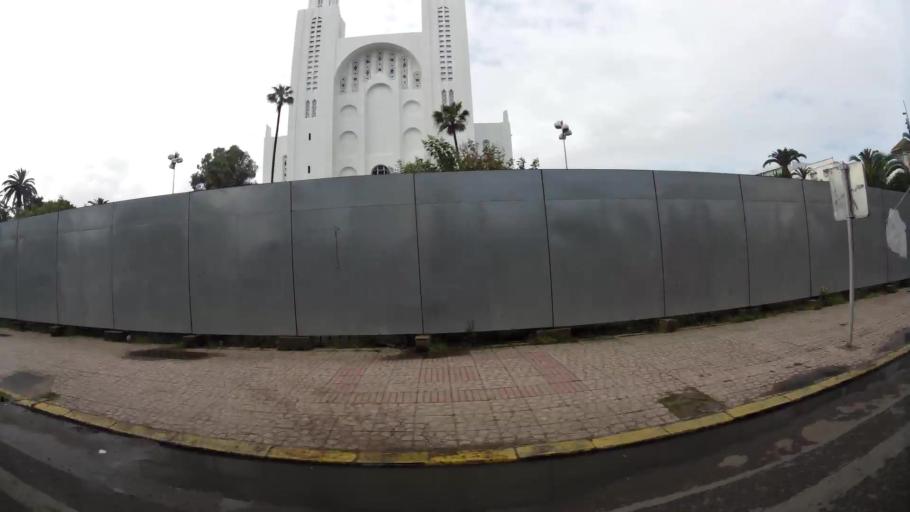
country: MA
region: Grand Casablanca
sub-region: Casablanca
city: Casablanca
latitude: 33.5919
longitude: -7.6242
